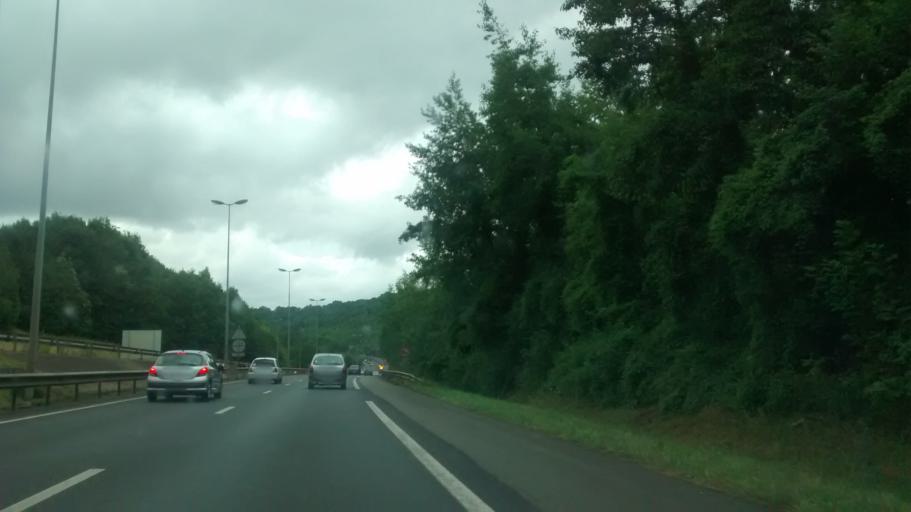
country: FR
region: Haute-Normandie
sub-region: Departement de la Seine-Maritime
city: Darnetal
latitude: 49.4534
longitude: 1.1450
